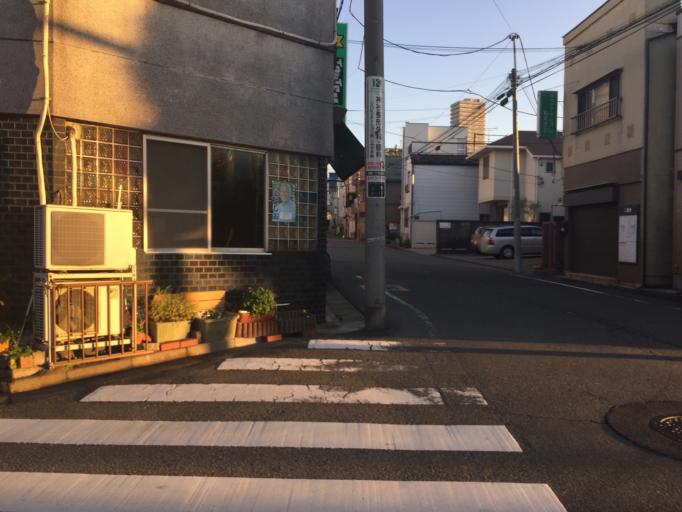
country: JP
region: Tokyo
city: Tokyo
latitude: 35.6366
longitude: 139.6591
